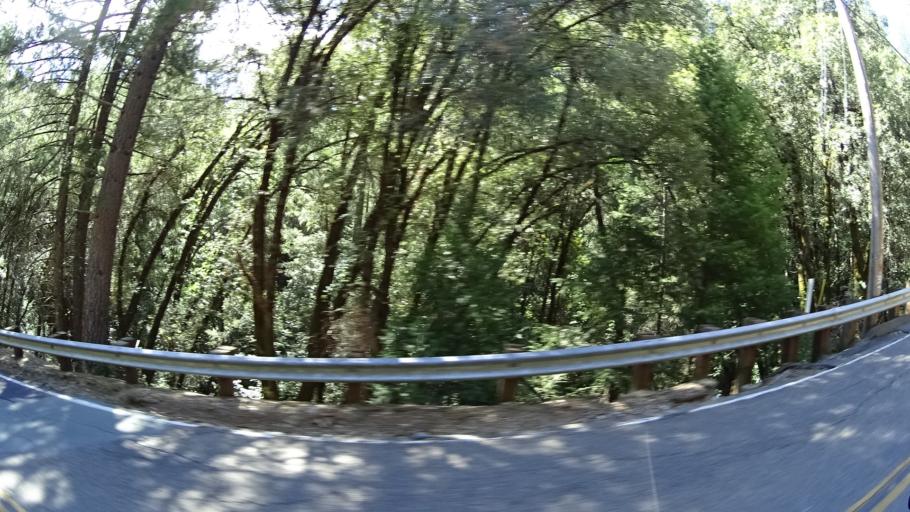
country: US
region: California
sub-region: Amador County
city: Pioneer
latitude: 38.3539
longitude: -120.5078
